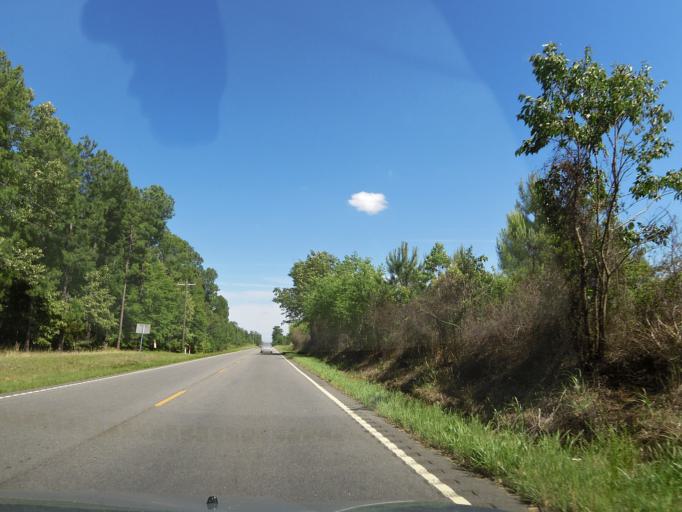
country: US
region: South Carolina
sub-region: Aiken County
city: Aiken
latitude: 33.5215
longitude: -81.6083
